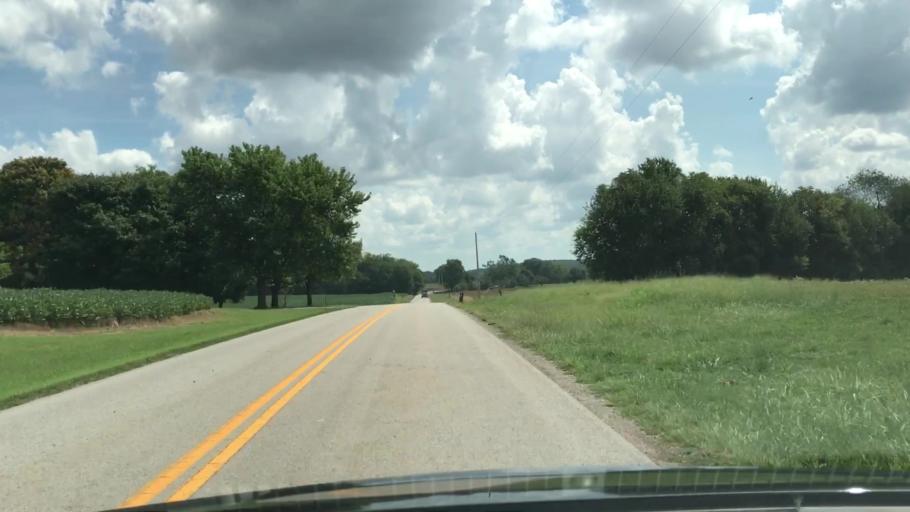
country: US
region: Kentucky
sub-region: Todd County
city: Guthrie
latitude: 36.7115
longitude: -87.0556
